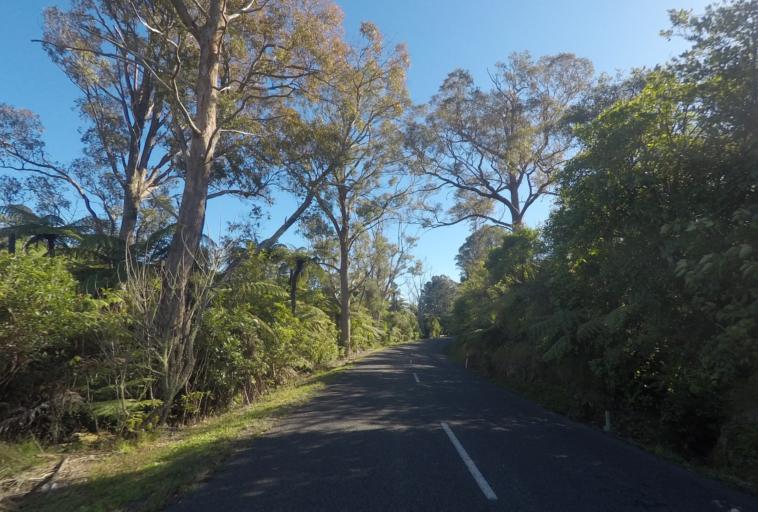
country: NZ
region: Bay of Plenty
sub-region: Western Bay of Plenty District
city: Waihi Beach
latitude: -37.3946
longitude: 175.9054
